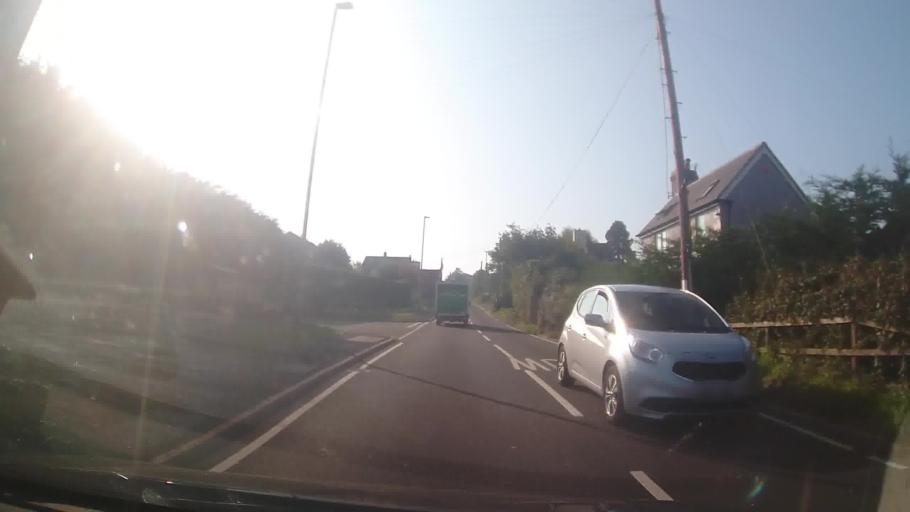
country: GB
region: England
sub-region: Shropshire
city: Harley
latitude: 52.6316
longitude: -2.6043
